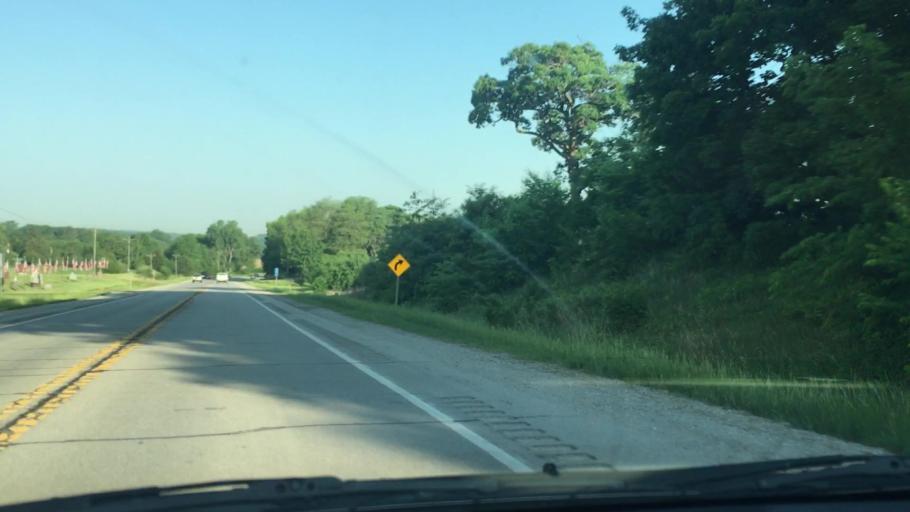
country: US
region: Iowa
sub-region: Johnson County
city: Tiffin
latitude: 41.7113
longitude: -91.6939
